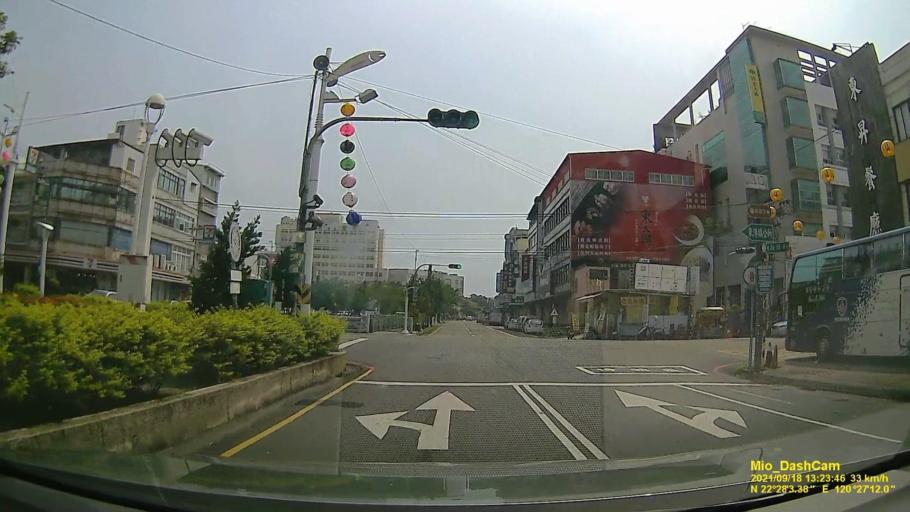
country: TW
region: Taiwan
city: Fengshan
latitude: 22.4677
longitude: 120.4534
